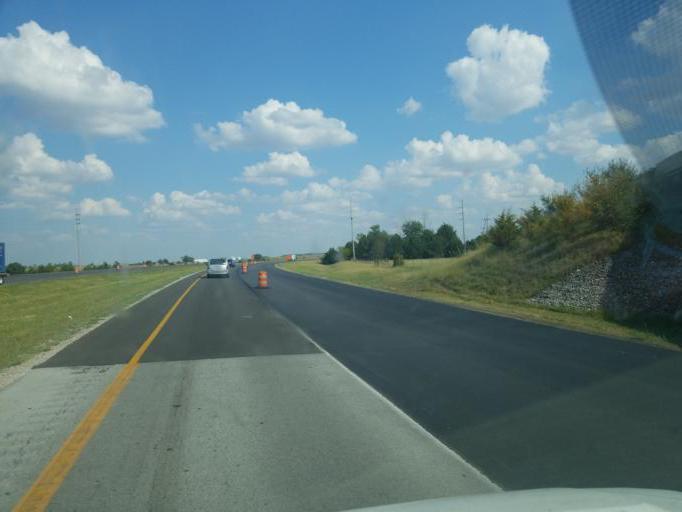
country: US
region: Ohio
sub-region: Allen County
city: Delphos
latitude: 40.8724
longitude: -84.4481
